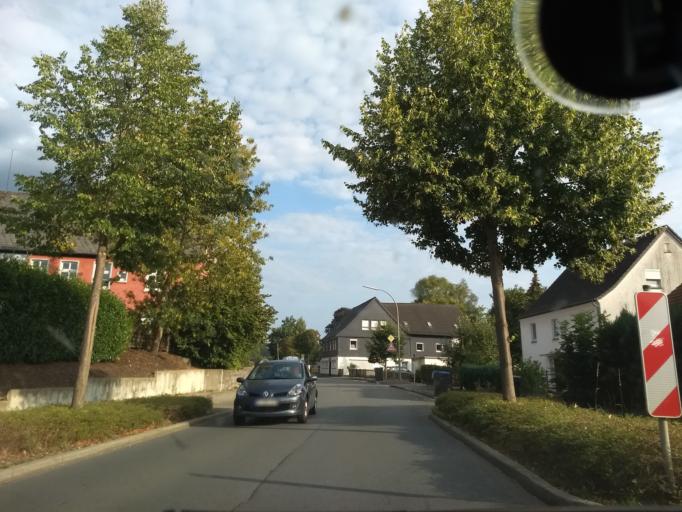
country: DE
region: North Rhine-Westphalia
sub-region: Regierungsbezirk Arnsberg
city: Arnsberg
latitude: 51.4023
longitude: 8.0862
